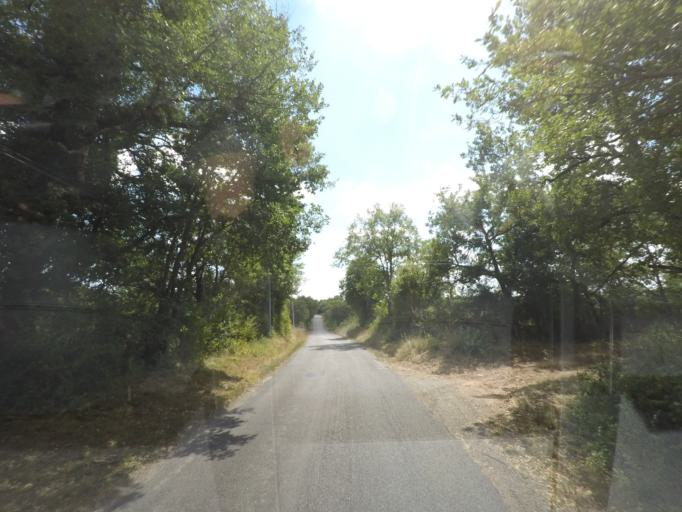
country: FR
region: Midi-Pyrenees
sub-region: Departement du Lot
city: Cajarc
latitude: 44.5673
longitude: 1.6705
